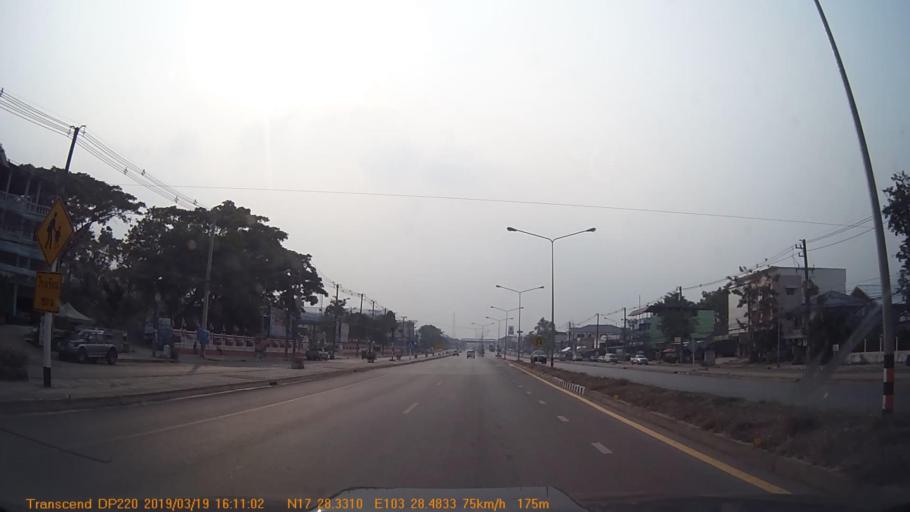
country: TH
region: Sakon Nakhon
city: Sawang Daen Din
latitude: 17.4723
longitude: 103.4741
